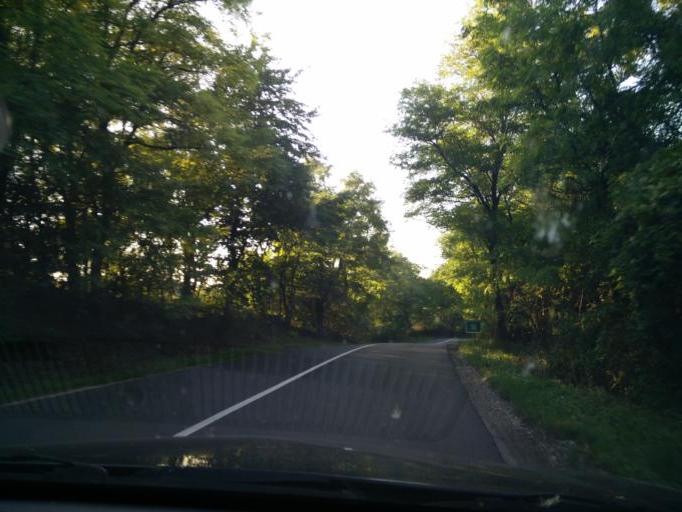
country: HU
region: Pest
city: Perbal
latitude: 47.6323
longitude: 18.7806
